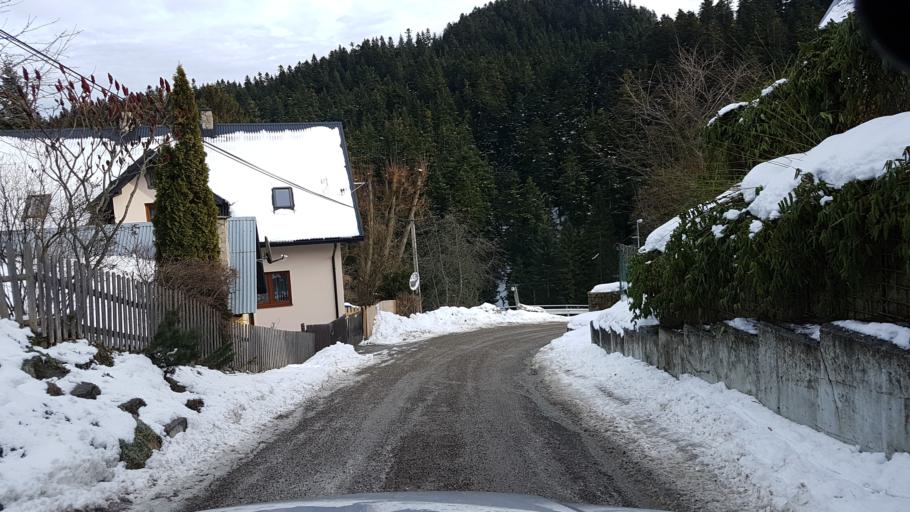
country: PL
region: Lesser Poland Voivodeship
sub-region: Powiat nowosadecki
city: Rytro
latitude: 49.4168
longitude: 20.6415
